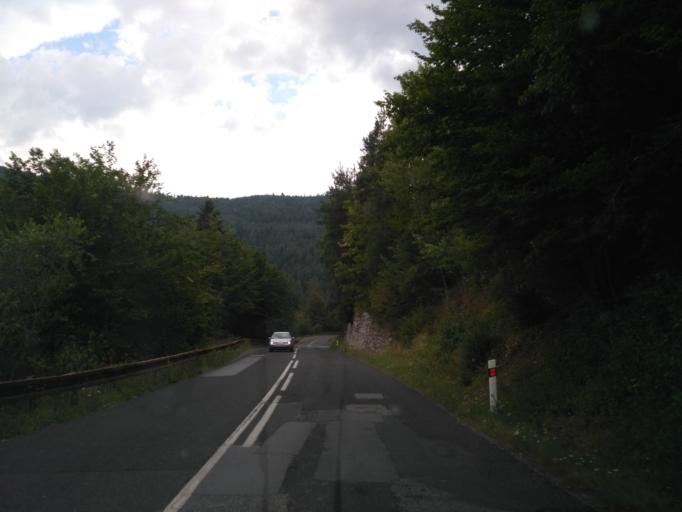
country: SK
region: Kosicky
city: Gelnica
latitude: 48.8368
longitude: 20.9230
